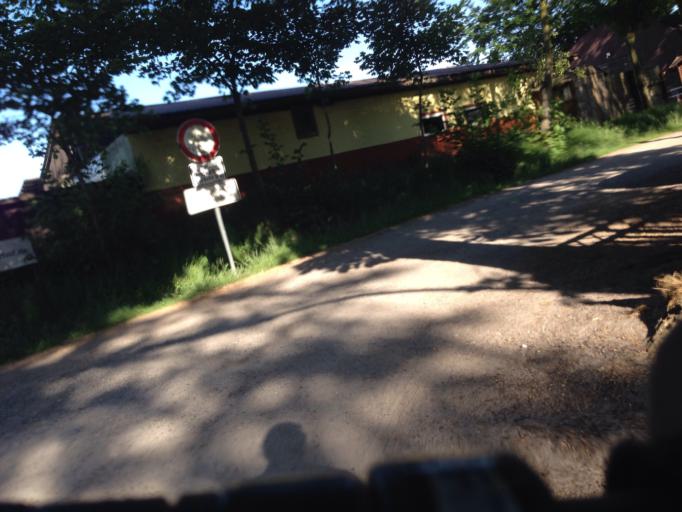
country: DE
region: Schleswig-Holstein
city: Stapelfeld
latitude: 53.5927
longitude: 10.1933
